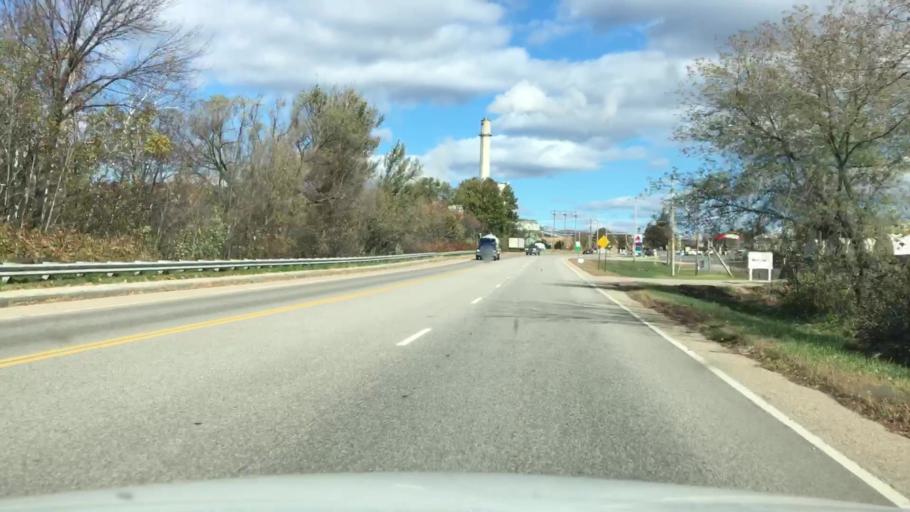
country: US
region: New Hampshire
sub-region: Coos County
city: Berlin
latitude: 44.4666
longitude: -71.1797
